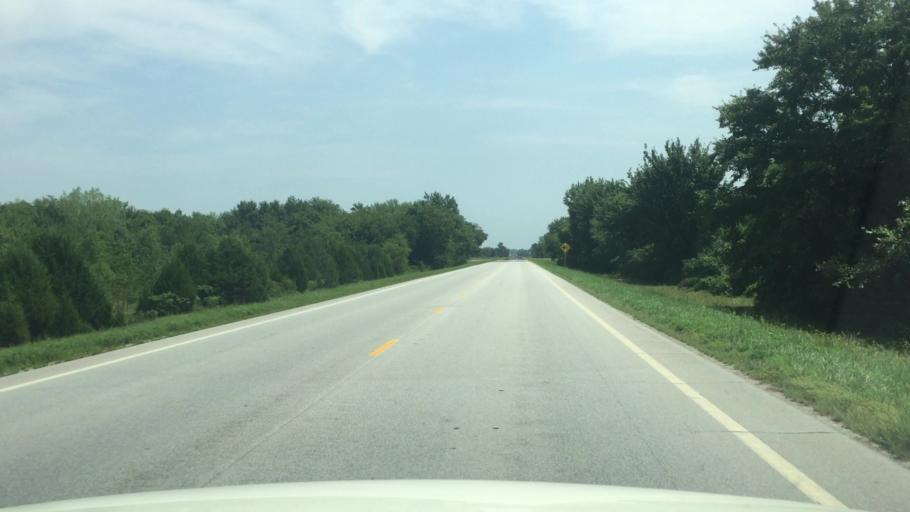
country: US
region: Kansas
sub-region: Cherokee County
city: Columbus
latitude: 37.1787
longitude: -94.8721
